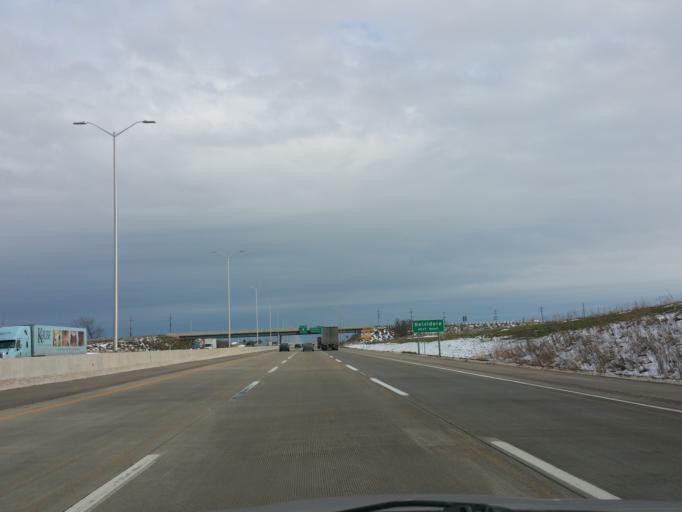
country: US
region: Illinois
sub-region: Boone County
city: Belvidere
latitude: 42.2337
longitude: -88.8224
